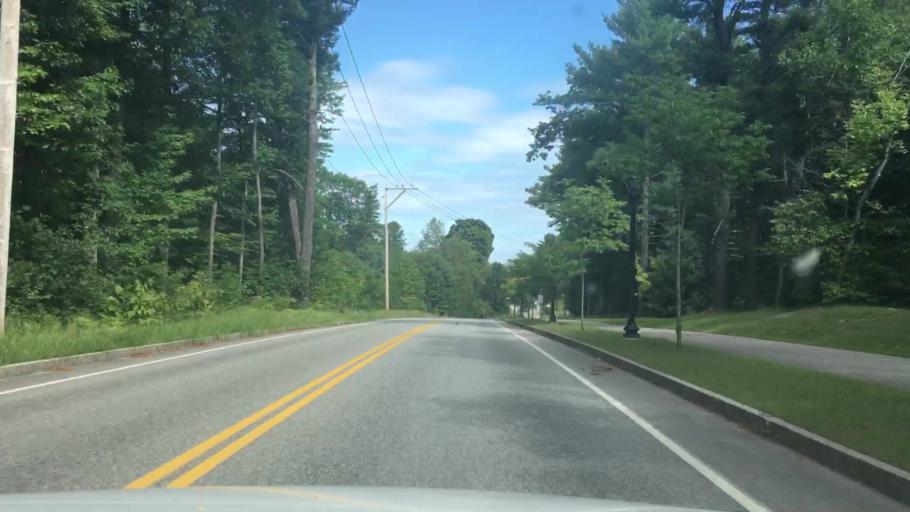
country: US
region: Maine
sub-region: Androscoggin County
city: Auburn
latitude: 44.0972
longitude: -70.2461
